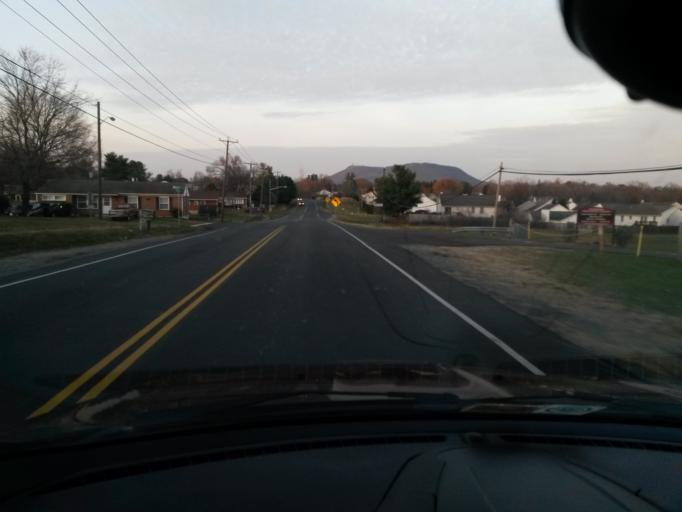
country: US
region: Virginia
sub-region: Roanoke County
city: Hollins
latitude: 37.3288
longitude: -79.9372
